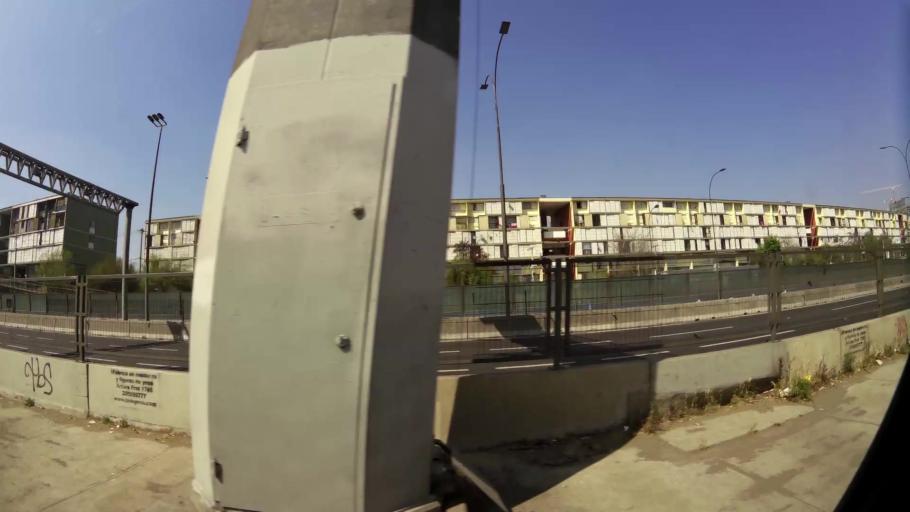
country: CL
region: Santiago Metropolitan
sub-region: Provincia de Santiago
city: Lo Prado
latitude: -33.4478
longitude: -70.6926
